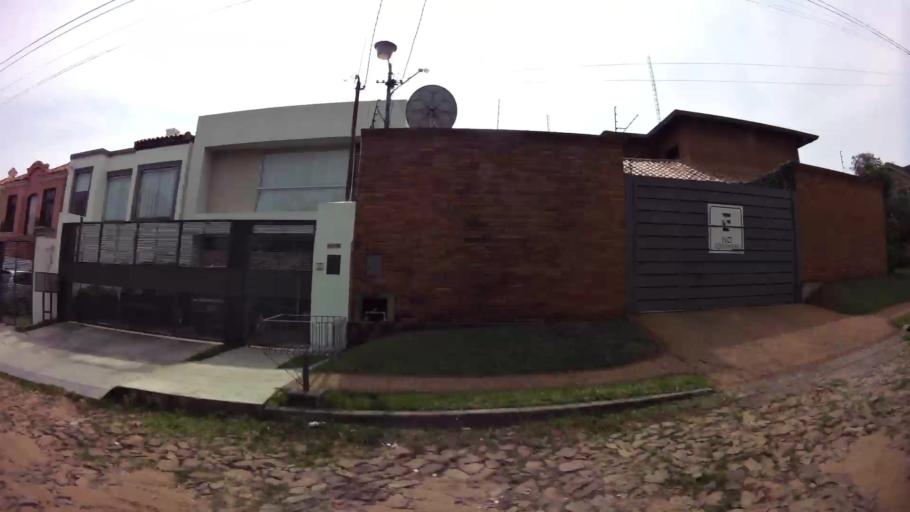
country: PY
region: Asuncion
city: Asuncion
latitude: -25.2717
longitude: -57.5679
